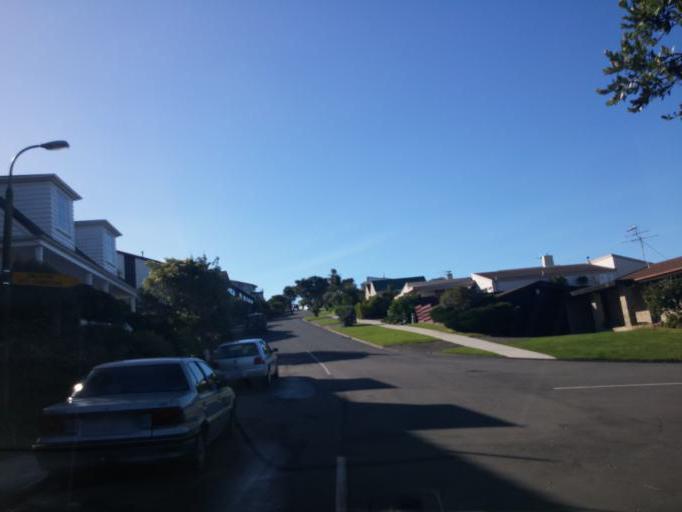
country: NZ
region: Wellington
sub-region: Wellington City
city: Wellington
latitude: -41.2546
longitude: 174.7842
